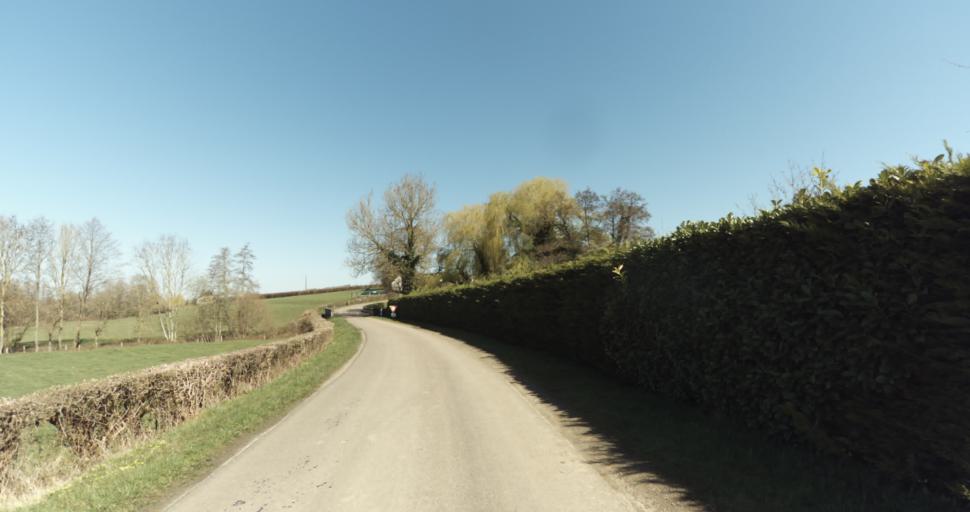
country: FR
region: Lower Normandy
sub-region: Departement du Calvados
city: Livarot
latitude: 49.0123
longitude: 0.0745
